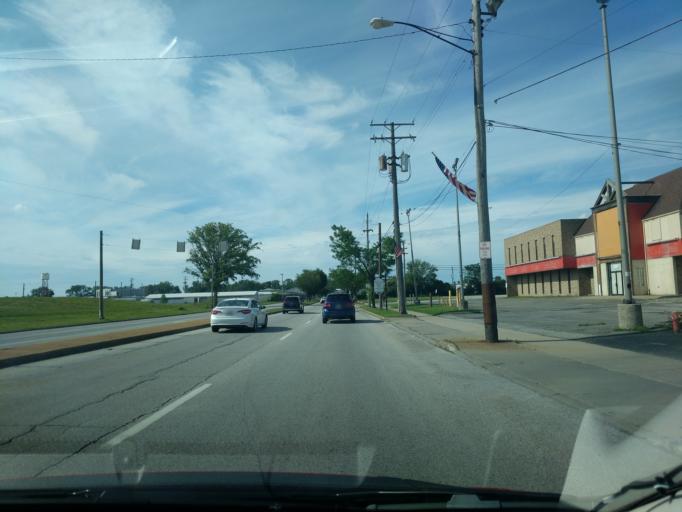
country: US
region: Ohio
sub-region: Cuyahoga County
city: North Randall
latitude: 41.4354
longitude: -81.5263
